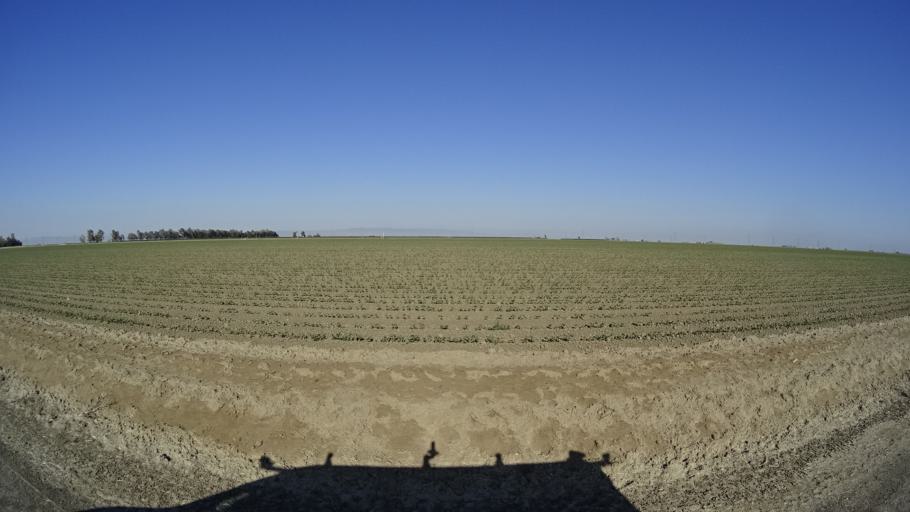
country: US
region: California
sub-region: Fresno County
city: Riverdale
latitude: 36.3835
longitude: -119.9277
